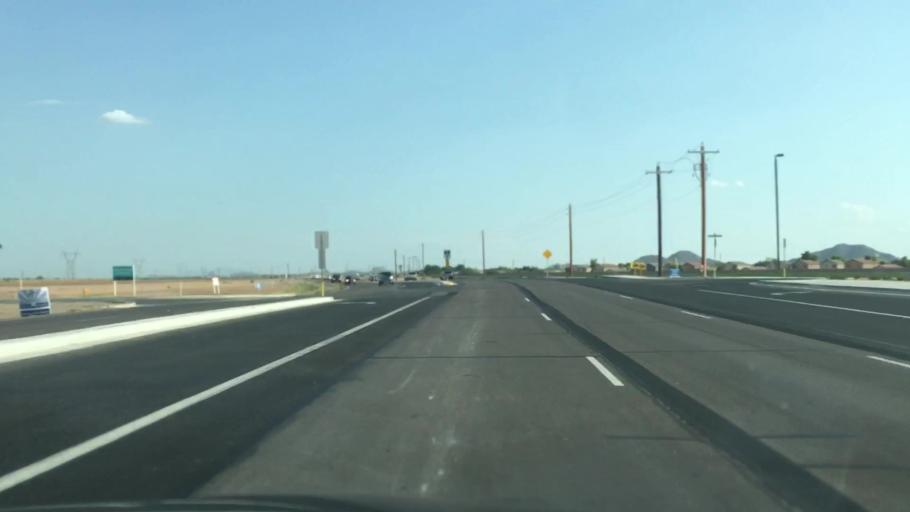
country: US
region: Arizona
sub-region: Pinal County
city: San Tan Valley
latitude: 33.2059
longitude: -111.5656
